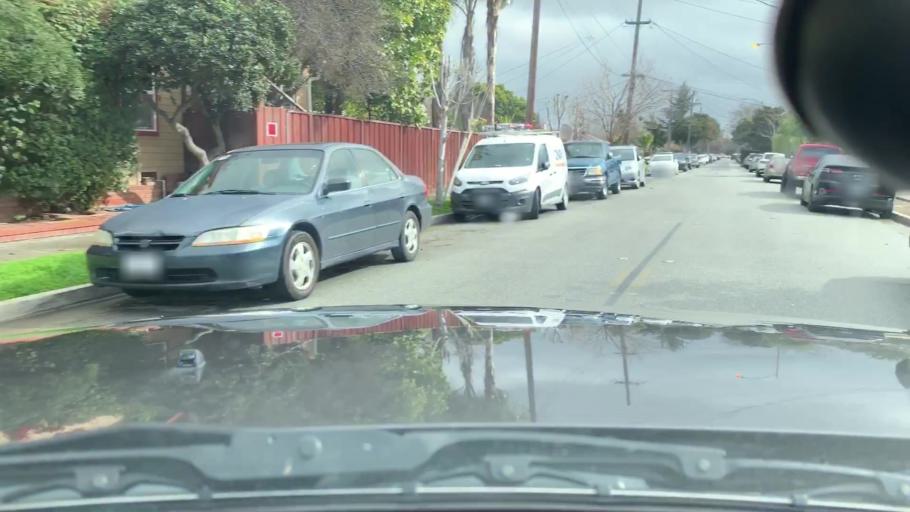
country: US
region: California
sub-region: Santa Clara County
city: San Jose
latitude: 37.3537
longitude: -121.8779
